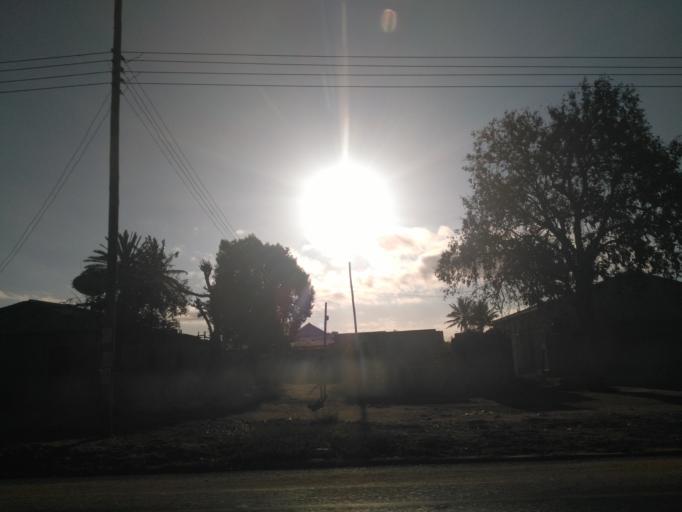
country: TZ
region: Dodoma
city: Dodoma
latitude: -6.1435
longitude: 35.7470
